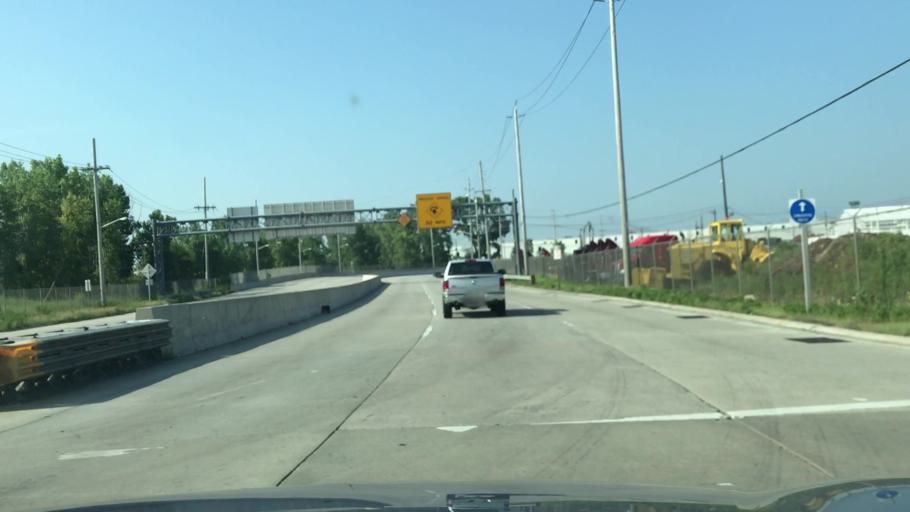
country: US
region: New Jersey
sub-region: Union County
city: Elizabeth
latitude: 40.6675
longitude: -74.1648
